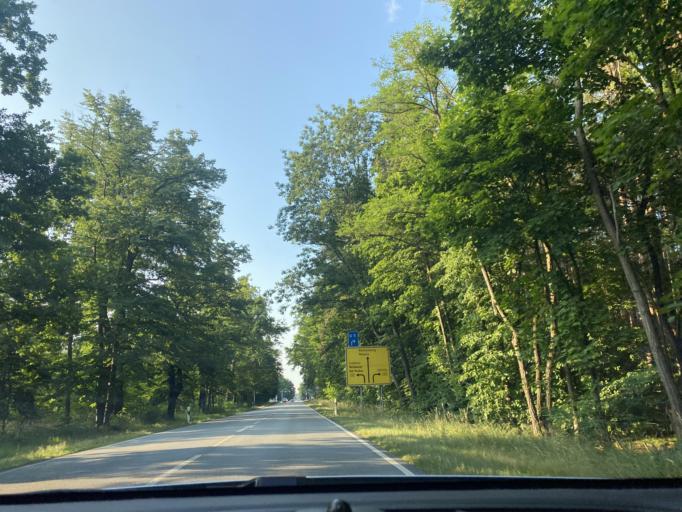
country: DE
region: Saxony
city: Niesky
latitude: 51.2766
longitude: 14.8176
